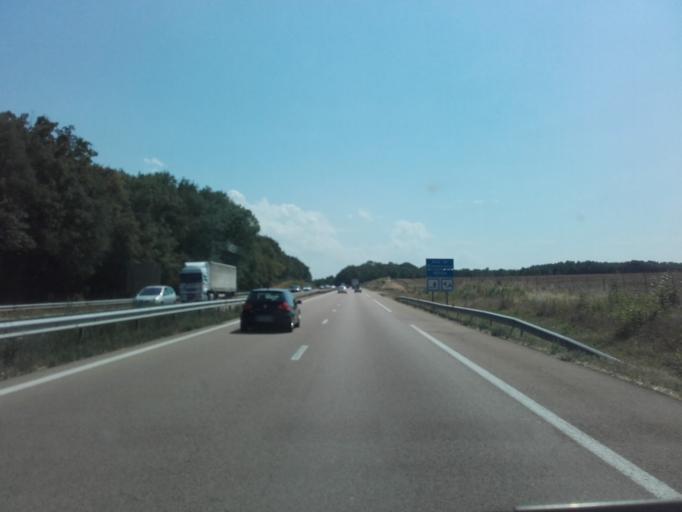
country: FR
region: Bourgogne
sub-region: Departement de l'Yonne
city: Joux-la-Ville
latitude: 47.6093
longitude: 3.9095
